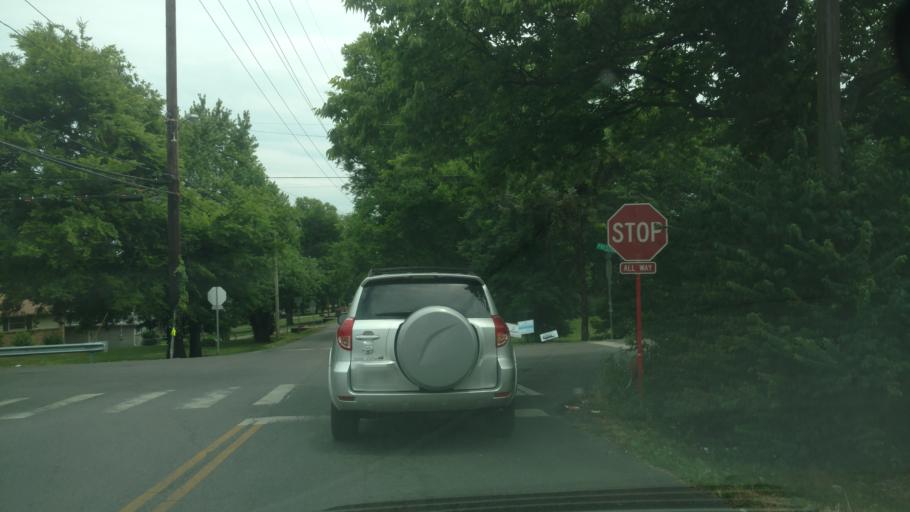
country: US
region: Tennessee
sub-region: Davidson County
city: Nashville
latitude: 36.1960
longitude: -86.7174
